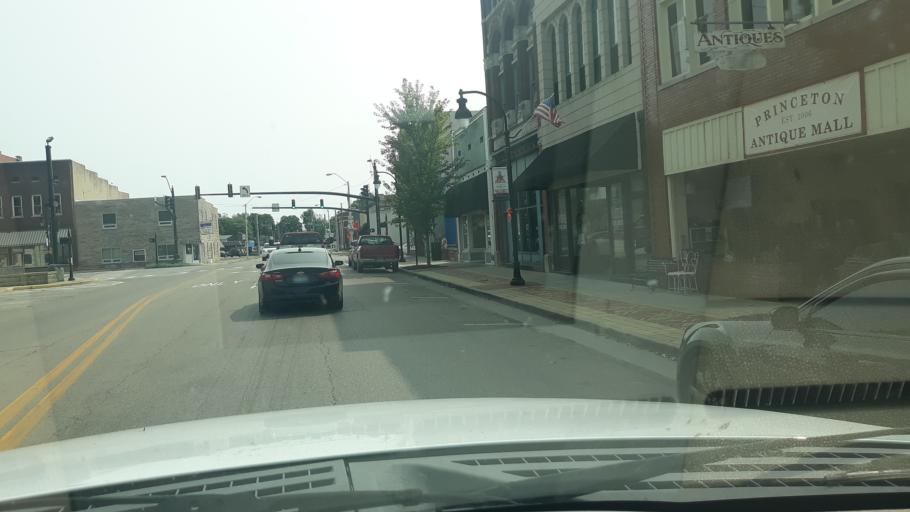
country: US
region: Indiana
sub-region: Gibson County
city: Princeton
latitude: 38.3552
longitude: -87.5684
